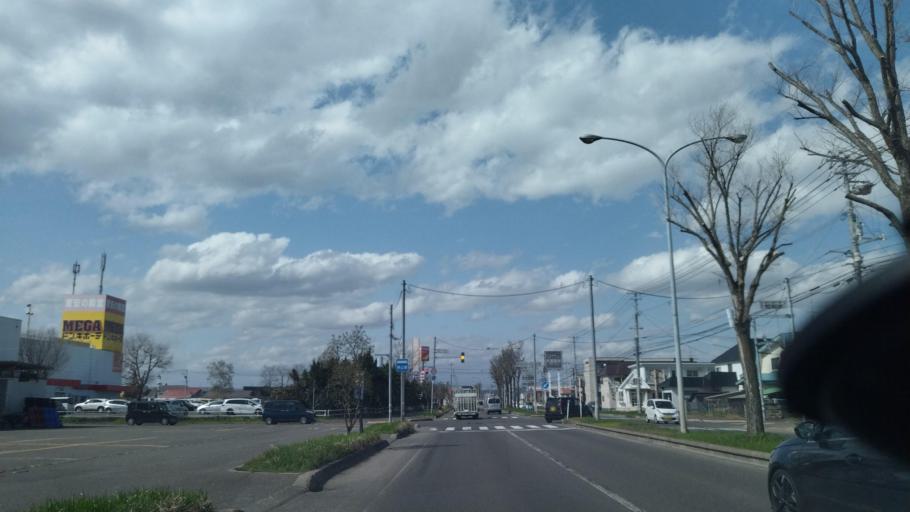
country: JP
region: Hokkaido
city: Obihiro
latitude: 42.9107
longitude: 143.1454
